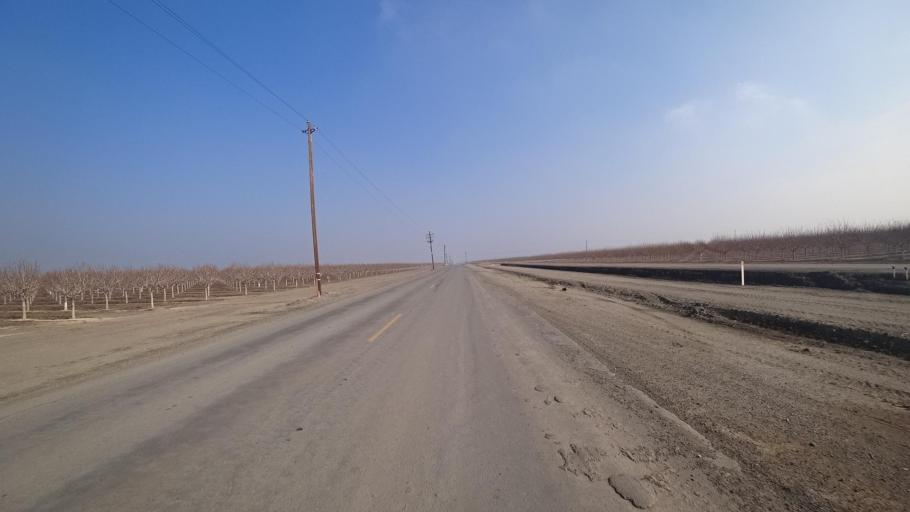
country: US
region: California
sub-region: Kern County
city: Greenfield
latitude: 35.1514
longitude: -119.0767
